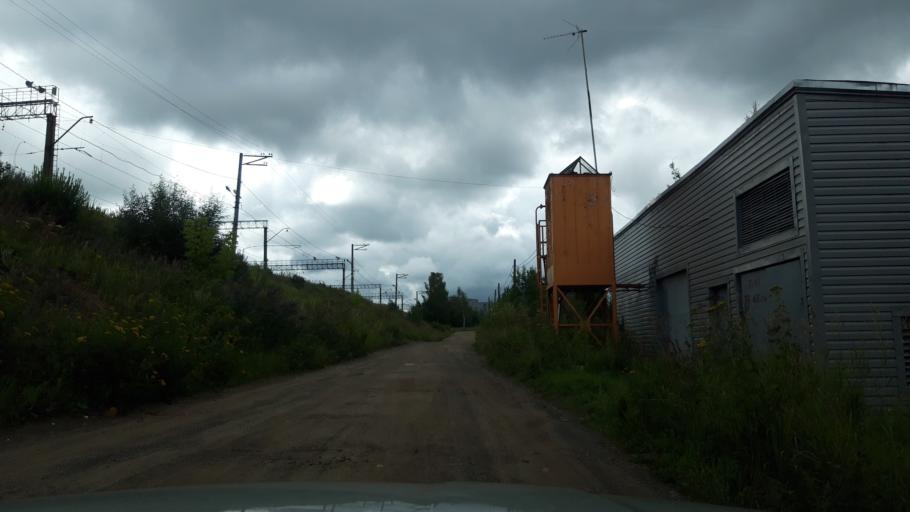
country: RU
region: Moskovskaya
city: Povarovo
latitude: 56.0492
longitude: 37.0564
